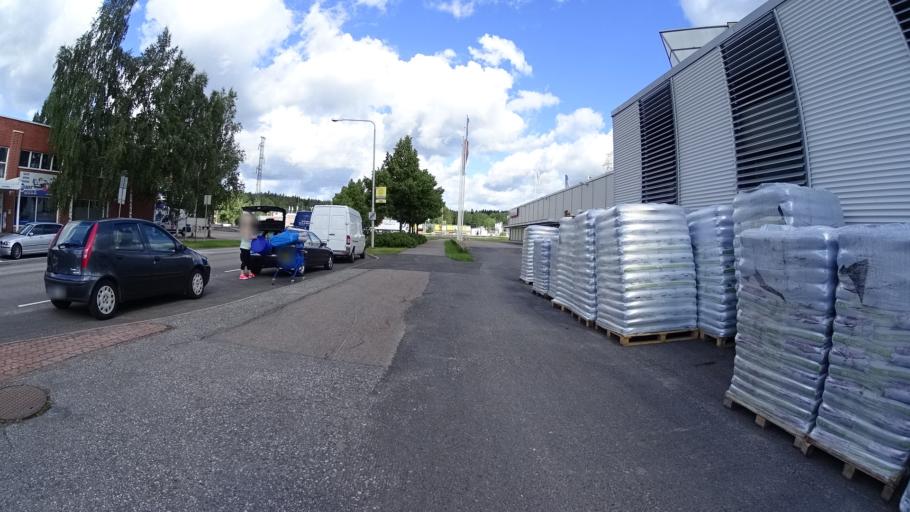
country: FI
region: Uusimaa
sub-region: Helsinki
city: Kilo
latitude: 60.2772
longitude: 24.8180
